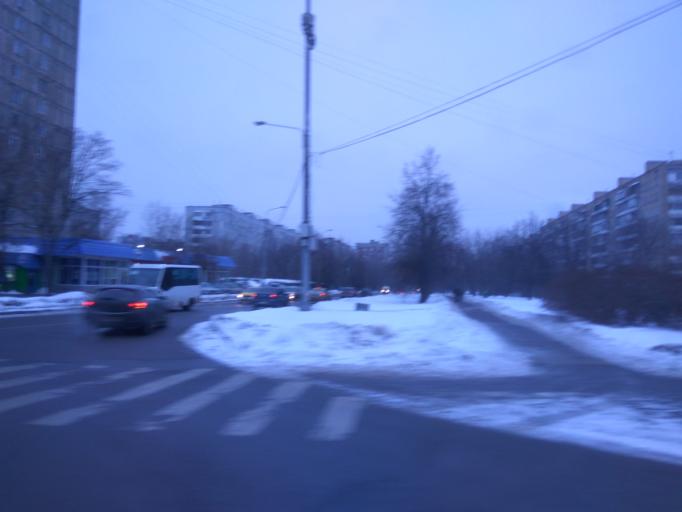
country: RU
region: Moscow
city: Gol'yanovo
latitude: 55.8177
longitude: 37.8270
